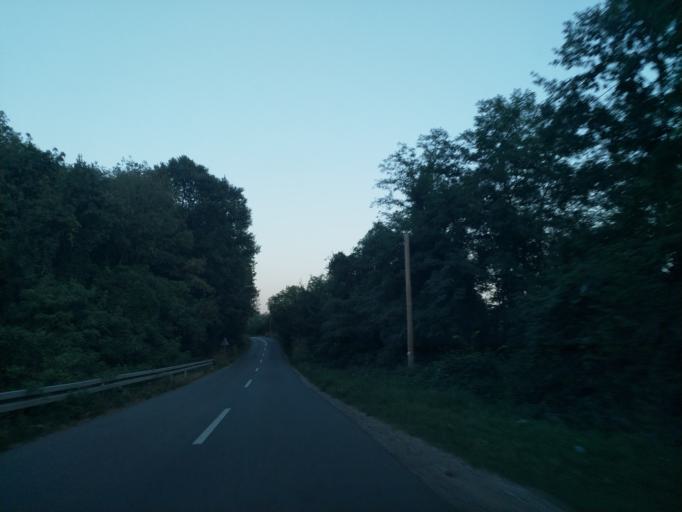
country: RS
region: Central Serbia
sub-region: Rasinski Okrug
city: Krusevac
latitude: 43.6208
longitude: 21.3196
